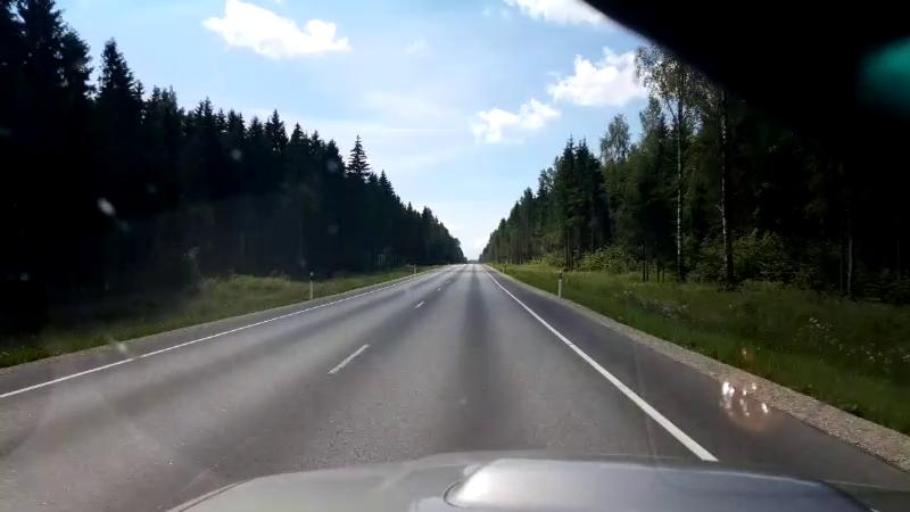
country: EE
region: Jaervamaa
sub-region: Paide linn
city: Paide
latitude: 58.9599
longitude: 25.6559
